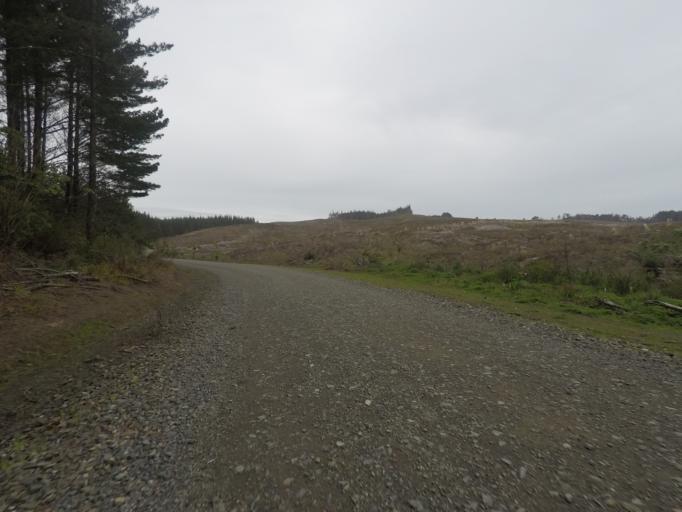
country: NZ
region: Auckland
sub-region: Auckland
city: Muriwai Beach
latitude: -36.7453
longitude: 174.5774
